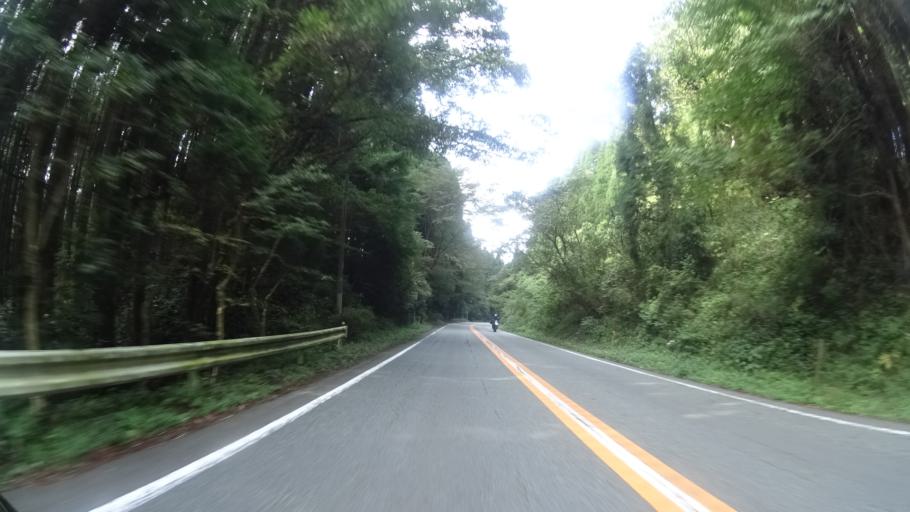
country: JP
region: Kumamoto
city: Aso
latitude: 33.0741
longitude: 131.0635
